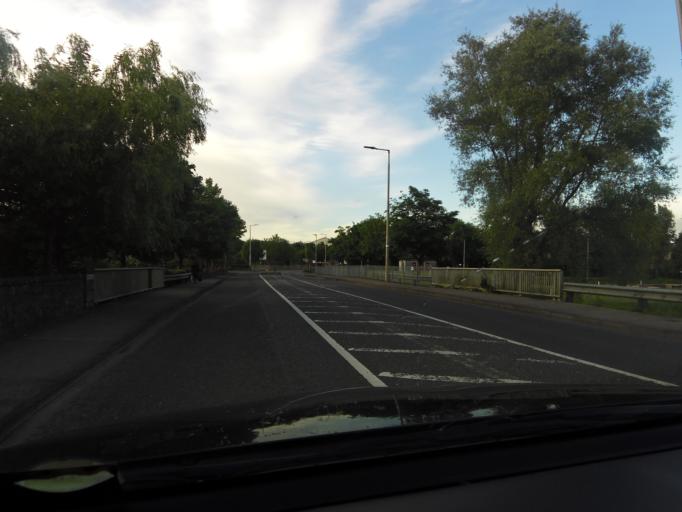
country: IE
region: Connaught
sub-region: County Galway
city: Ballinasloe
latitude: 53.3284
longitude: -8.2189
